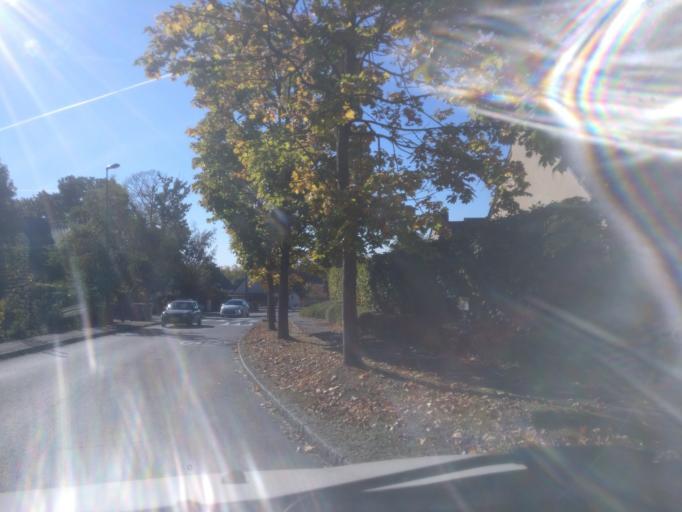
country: FR
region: Brittany
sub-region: Departement d'Ille-et-Vilaine
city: Chevaigne
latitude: 48.2081
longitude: -1.6316
